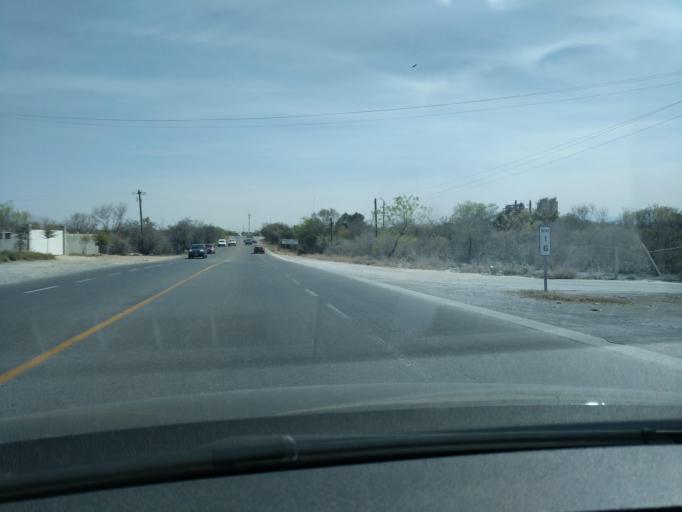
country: MX
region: Nuevo Leon
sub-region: Salinas Victoria
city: Las Torres
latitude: 25.9203
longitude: -100.3687
